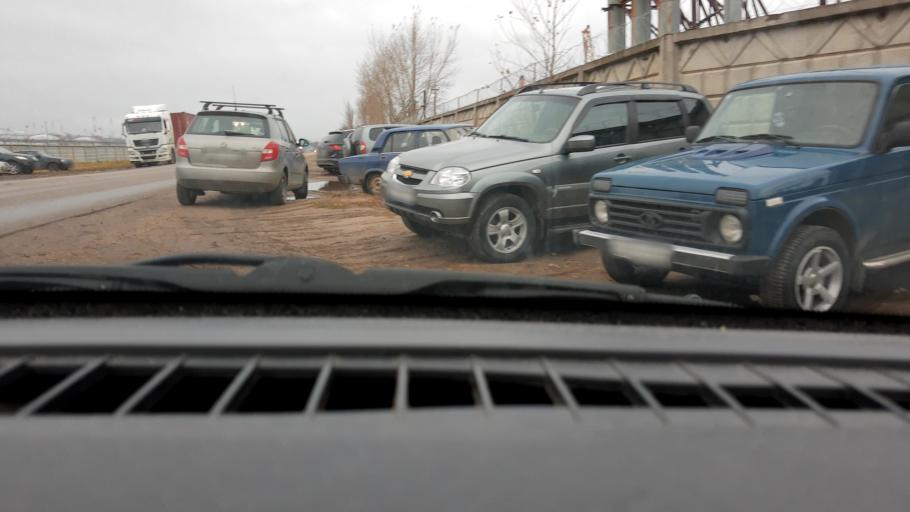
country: RU
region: Nizjnij Novgorod
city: Kstovo
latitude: 56.1221
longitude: 44.1347
